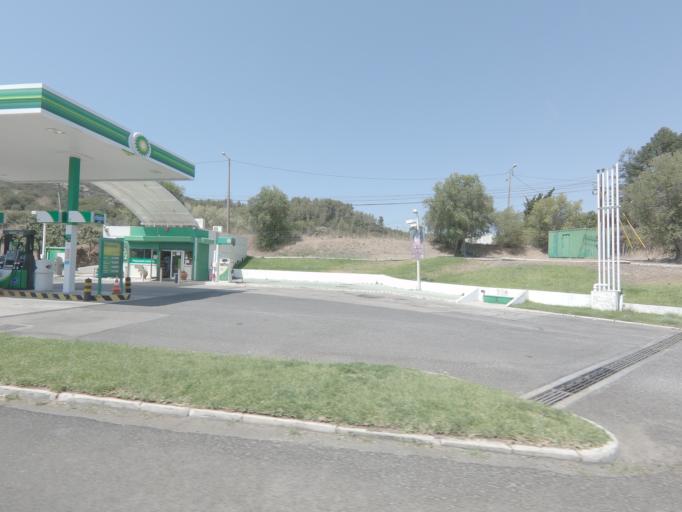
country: PT
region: Setubal
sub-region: Setubal
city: Setubal
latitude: 38.5318
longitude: -8.9161
